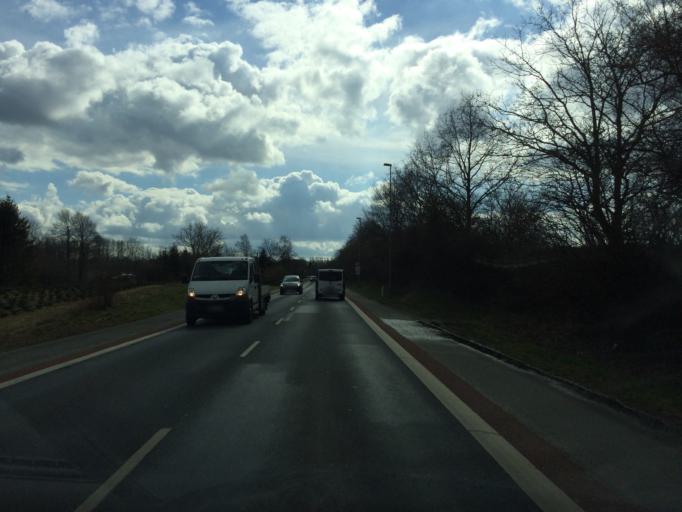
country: DK
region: South Denmark
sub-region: Nordfyns Kommune
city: Sonderso
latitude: 55.4013
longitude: 10.2605
